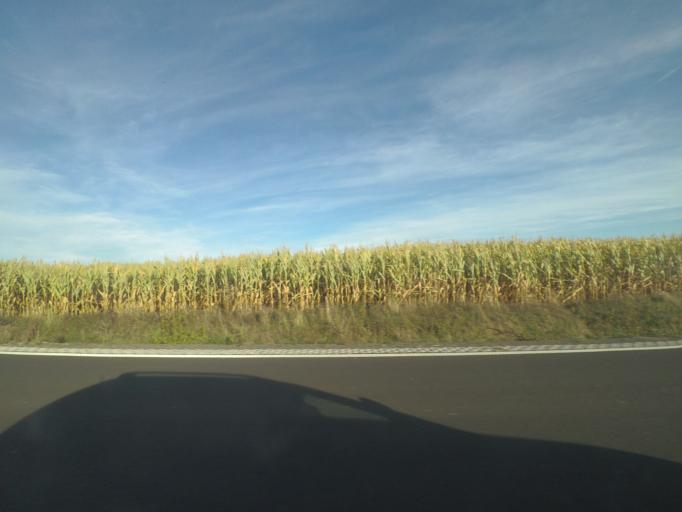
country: DE
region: Hesse
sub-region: Regierungsbezirk Giessen
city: Freiensteinau
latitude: 50.3819
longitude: 9.4290
